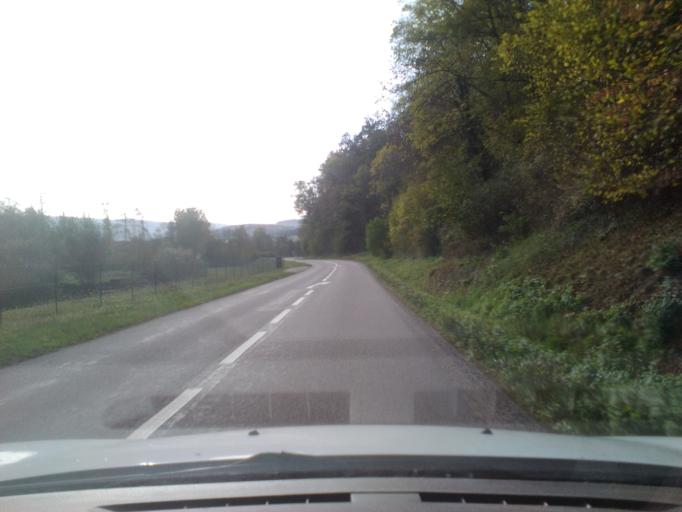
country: FR
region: Lorraine
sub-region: Departement des Vosges
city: Ban-de-Laveline
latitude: 48.2858
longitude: 7.0550
